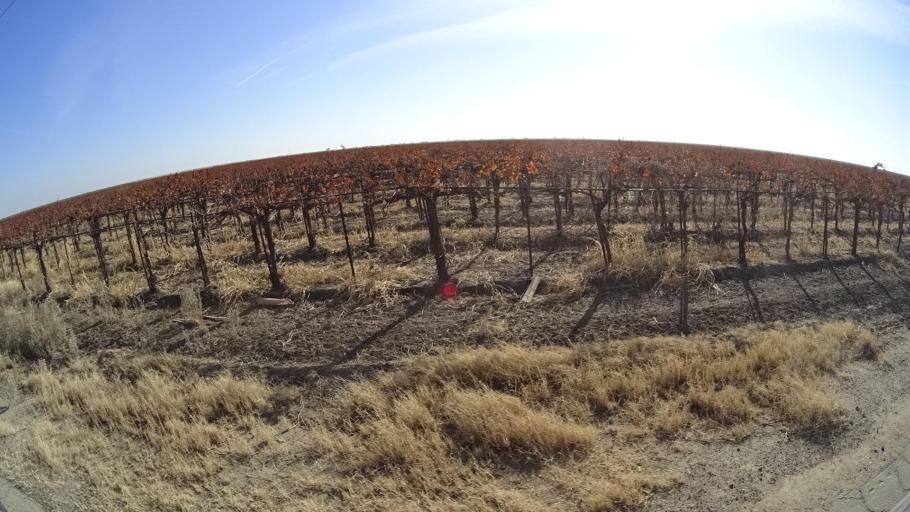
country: US
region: California
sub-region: Kern County
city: Wasco
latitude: 35.7032
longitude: -119.3411
